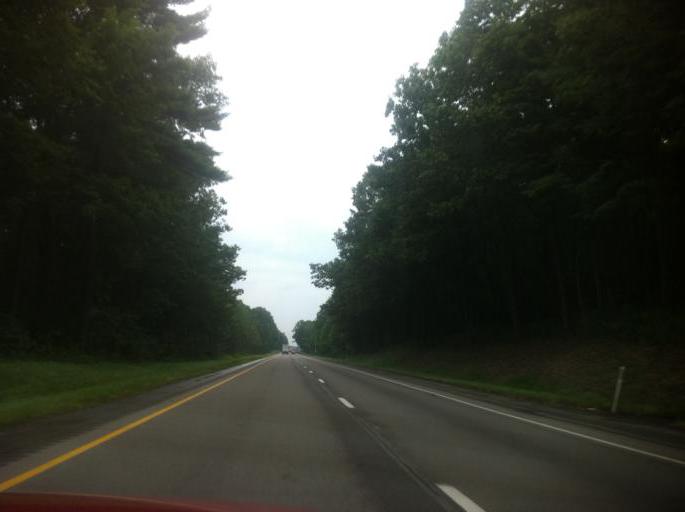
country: US
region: Pennsylvania
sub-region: Jefferson County
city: Brookville
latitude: 41.1799
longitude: -79.1298
